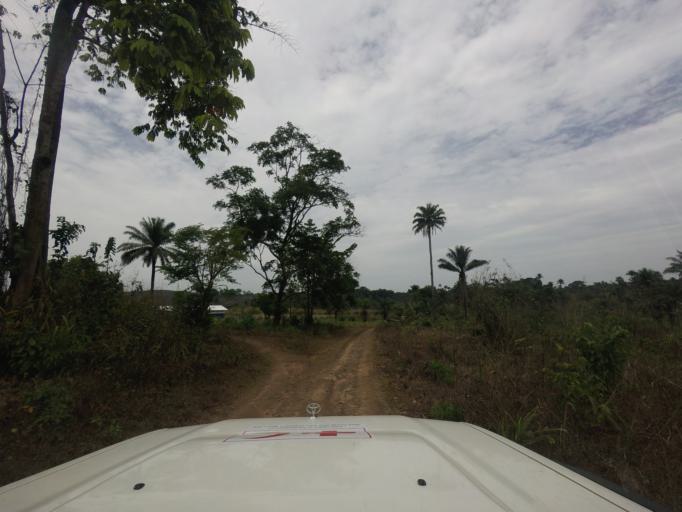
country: SL
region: Eastern Province
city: Buedu
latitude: 8.4237
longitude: -10.2636
